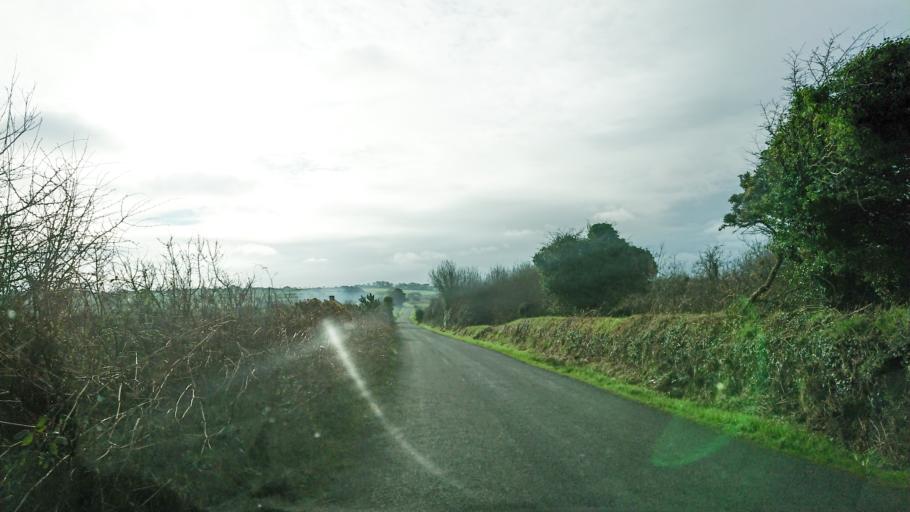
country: IE
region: Munster
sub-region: Waterford
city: Tra Mhor
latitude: 52.1665
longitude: -7.1868
